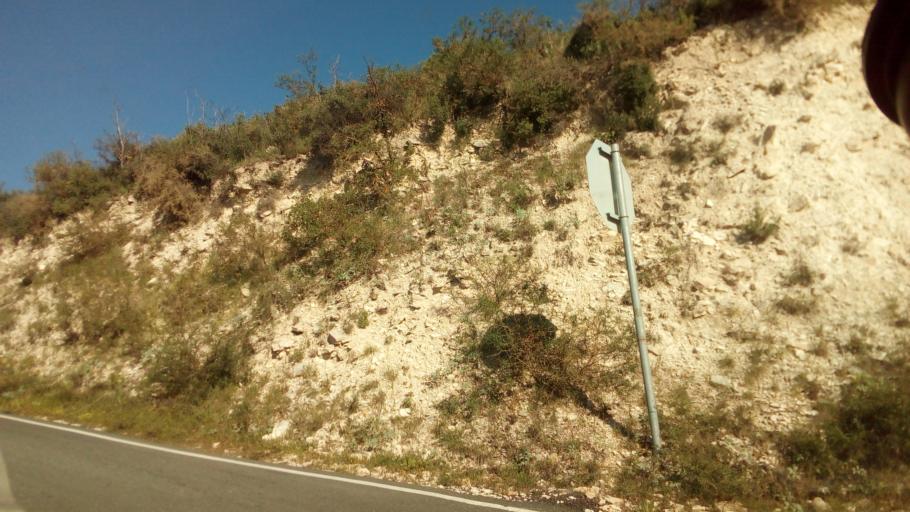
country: CY
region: Limassol
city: Pachna
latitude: 34.8580
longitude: 32.7606
